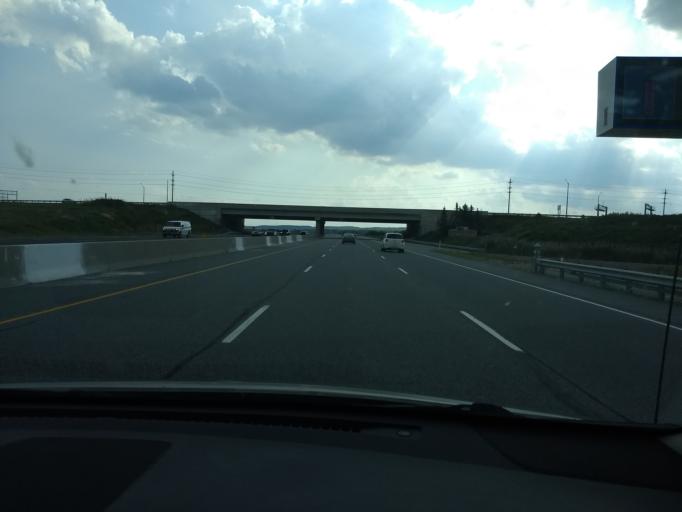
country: CA
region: Ontario
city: Burlington
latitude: 43.4166
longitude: -79.8191
